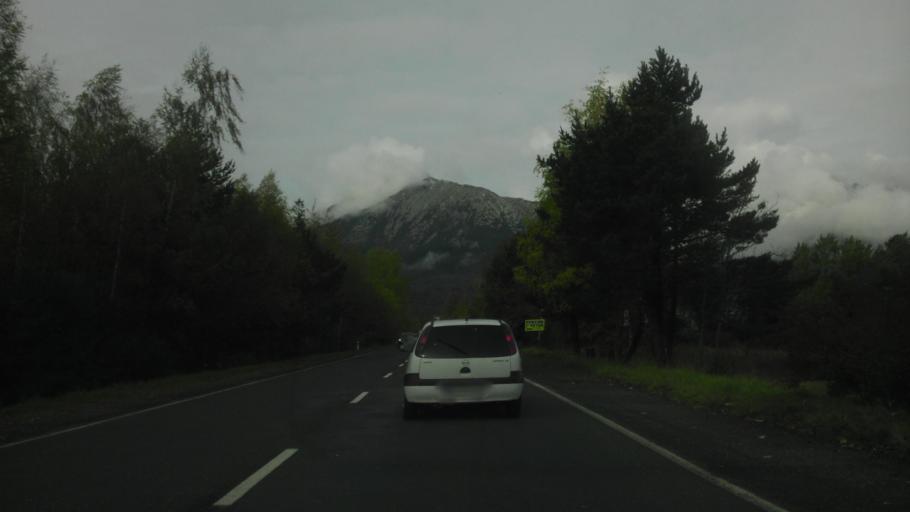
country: SK
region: Presovsky
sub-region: Okres Poprad
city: Vysoke Tatry
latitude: 49.1220
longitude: 20.2486
